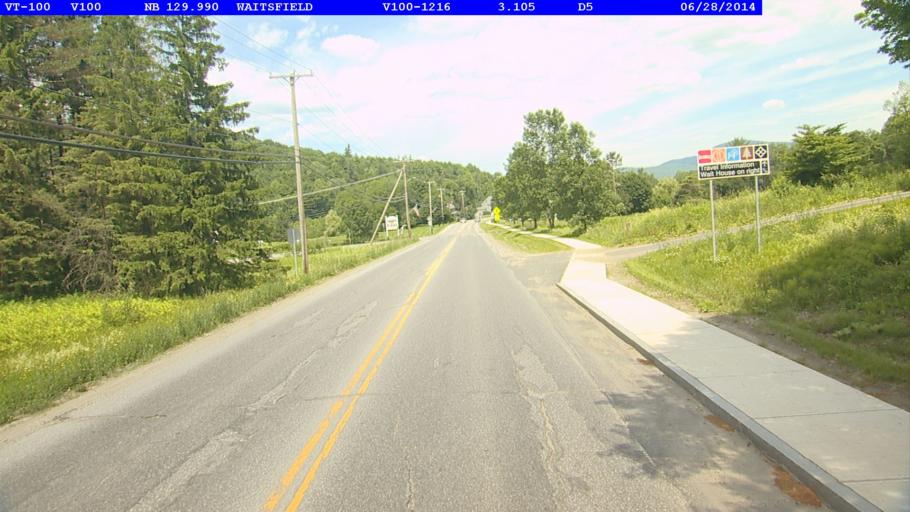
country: US
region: Vermont
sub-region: Washington County
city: Waterbury
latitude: 44.1864
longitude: -72.8335
